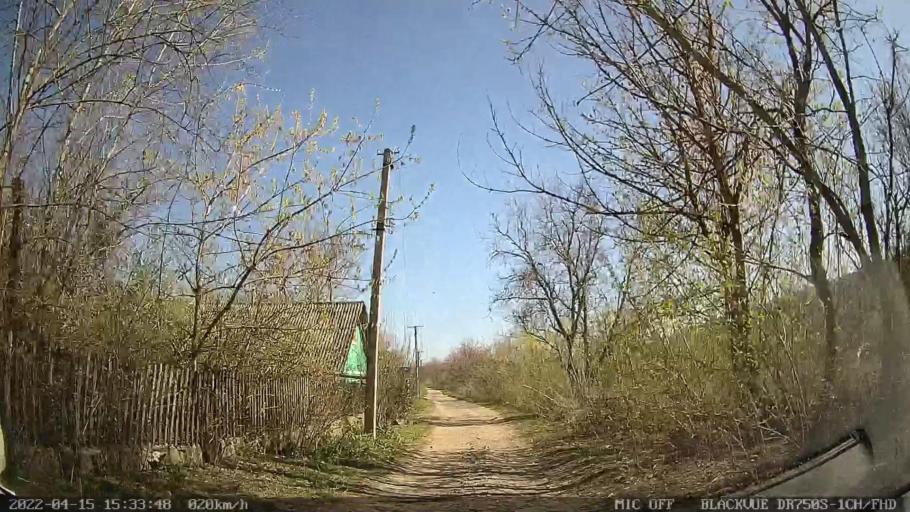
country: MD
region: Raionul Ocnita
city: Otaci
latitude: 48.3488
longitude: 27.9248
